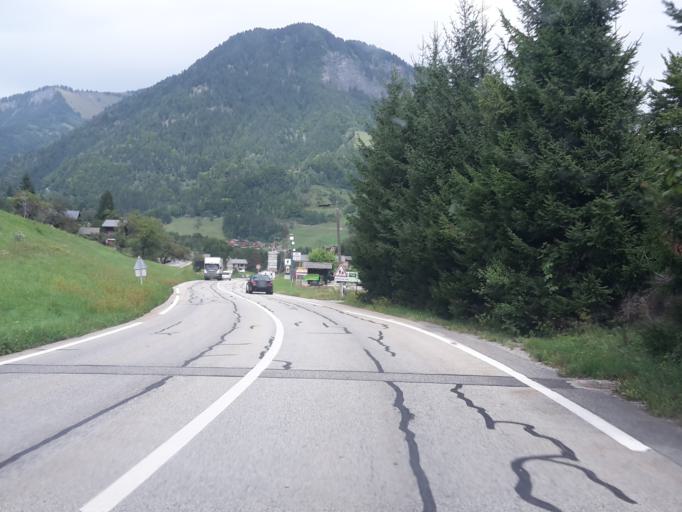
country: FR
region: Rhone-Alpes
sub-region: Departement de la Haute-Savoie
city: Praz-sur-Arly
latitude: 45.8097
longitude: 6.5054
